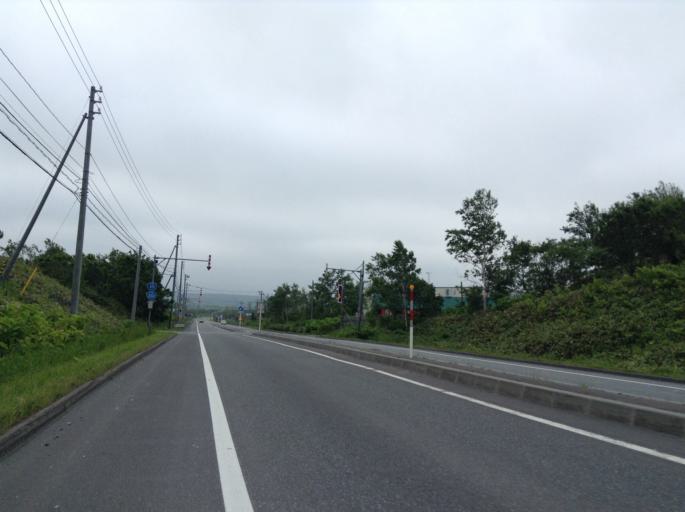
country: JP
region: Hokkaido
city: Wakkanai
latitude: 45.3729
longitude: 141.7182
